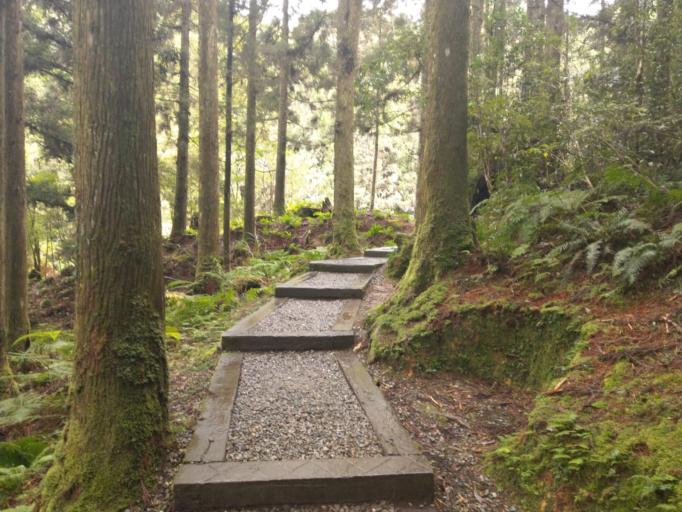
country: TW
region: Taiwan
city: Lugu
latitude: 23.6330
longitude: 120.7934
